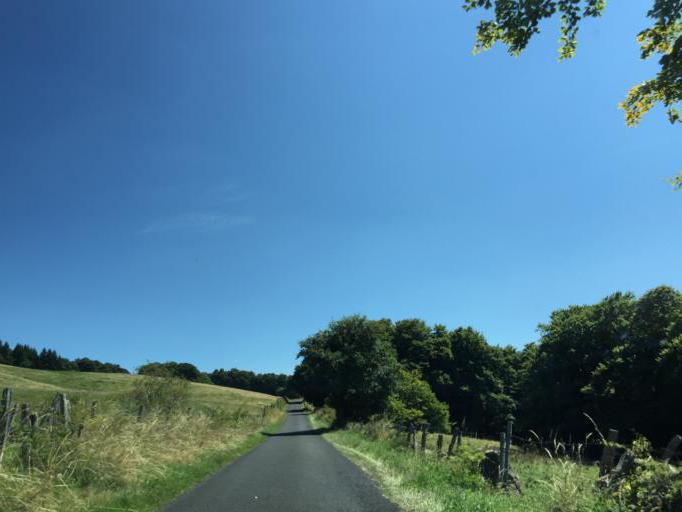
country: FR
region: Midi-Pyrenees
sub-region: Departement de l'Aveyron
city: Laguiole
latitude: 44.6528
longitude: 2.9179
